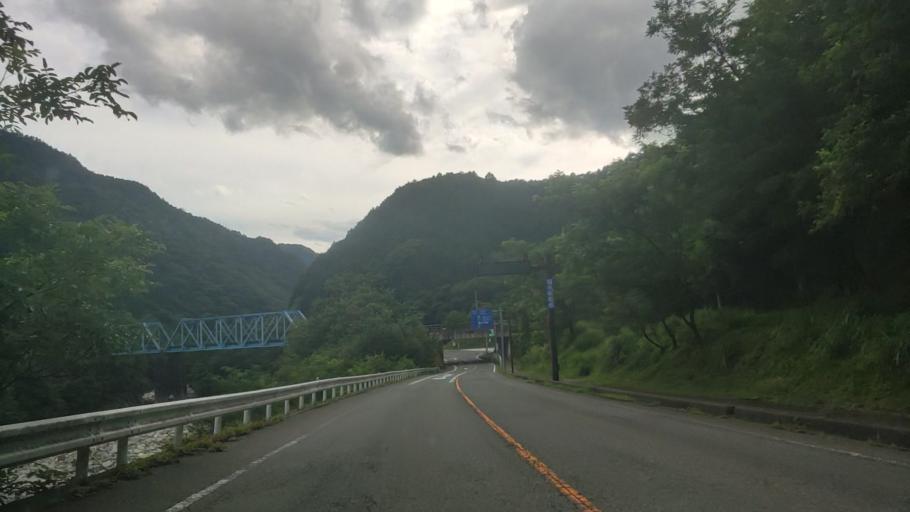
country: JP
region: Tochigi
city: Nikko
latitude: 36.6236
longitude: 139.4281
